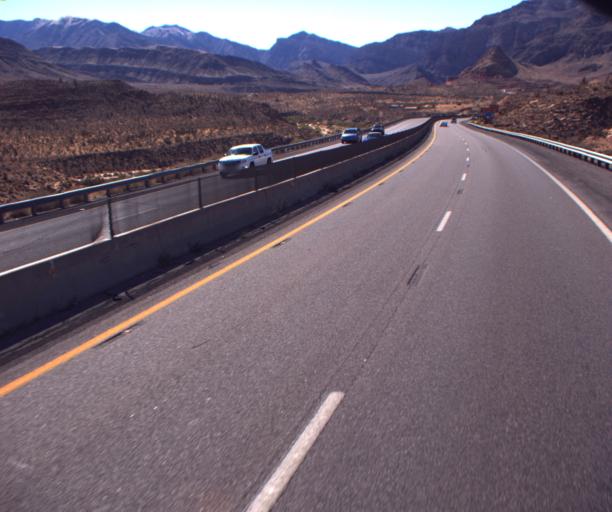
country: US
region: Arizona
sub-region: Mohave County
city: Beaver Dam
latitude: 36.9595
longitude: -113.7837
